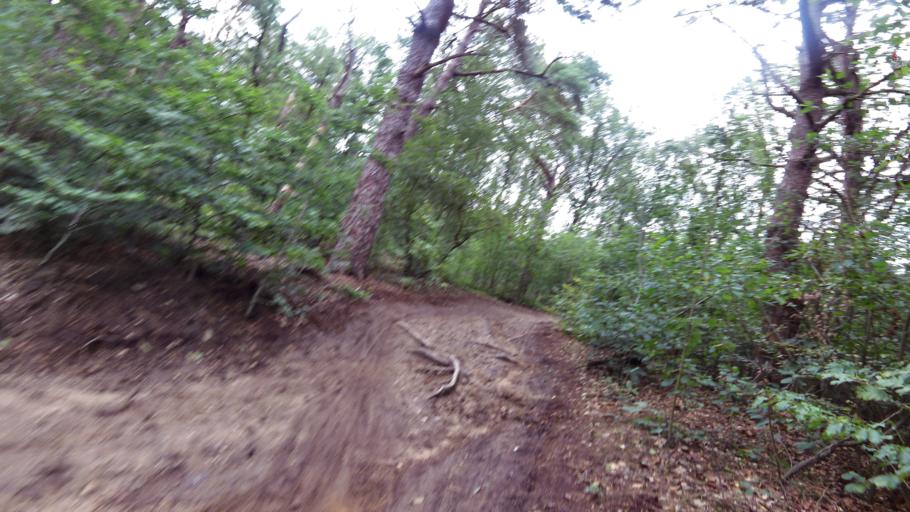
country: NL
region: Utrecht
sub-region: Gemeente Utrechtse Heuvelrug
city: Amerongen
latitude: 52.0062
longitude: 5.4709
